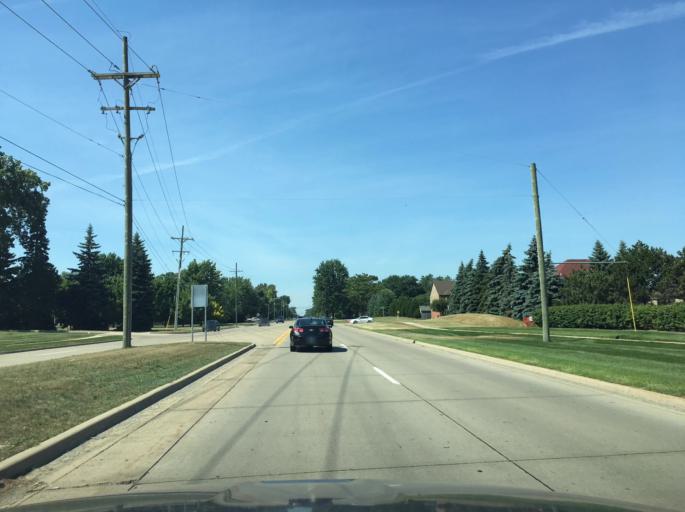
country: US
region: Michigan
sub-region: Macomb County
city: Utica
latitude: 42.6351
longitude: -82.9933
